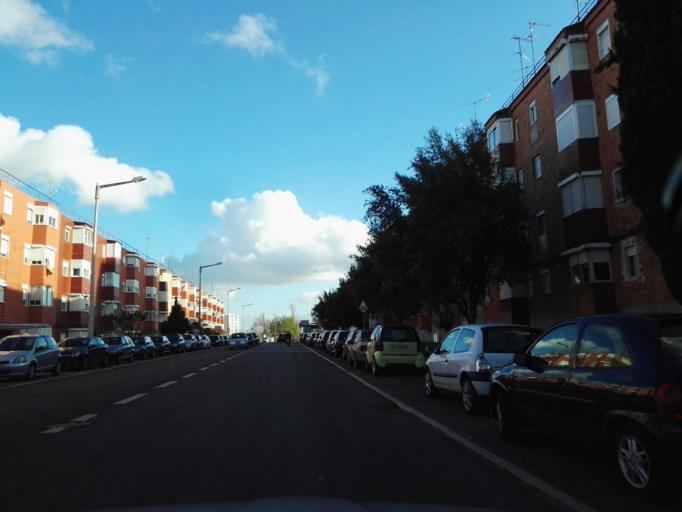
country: PT
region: Lisbon
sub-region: Loures
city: Moscavide
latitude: 38.7724
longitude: -9.1103
